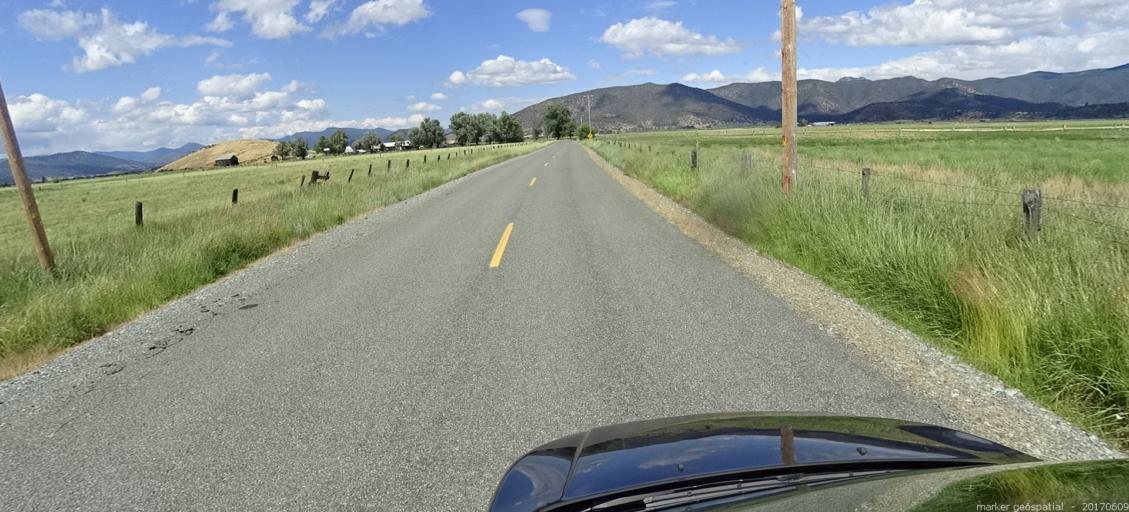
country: US
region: California
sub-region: Siskiyou County
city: Yreka
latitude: 41.4857
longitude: -122.8751
